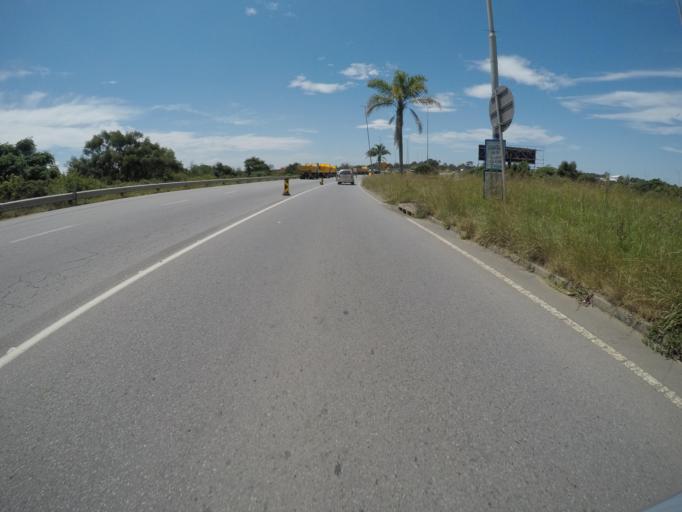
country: ZA
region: Eastern Cape
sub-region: Buffalo City Metropolitan Municipality
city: East London
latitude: -33.0373
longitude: 27.8334
